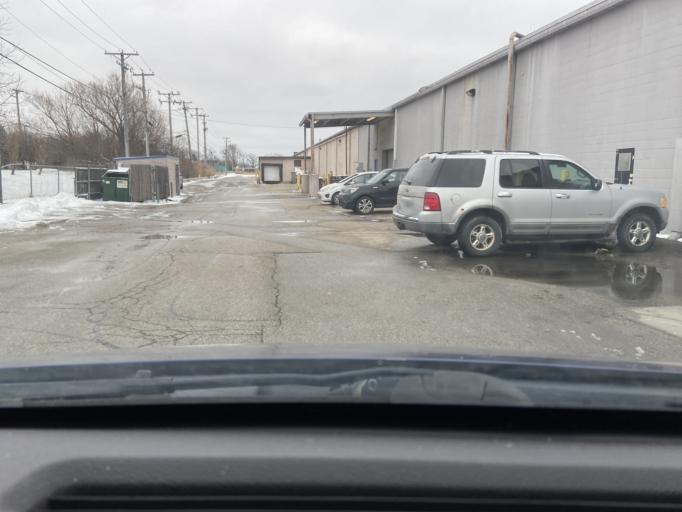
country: US
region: Illinois
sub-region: Lake County
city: Venetian Village
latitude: 42.3824
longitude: -88.0628
